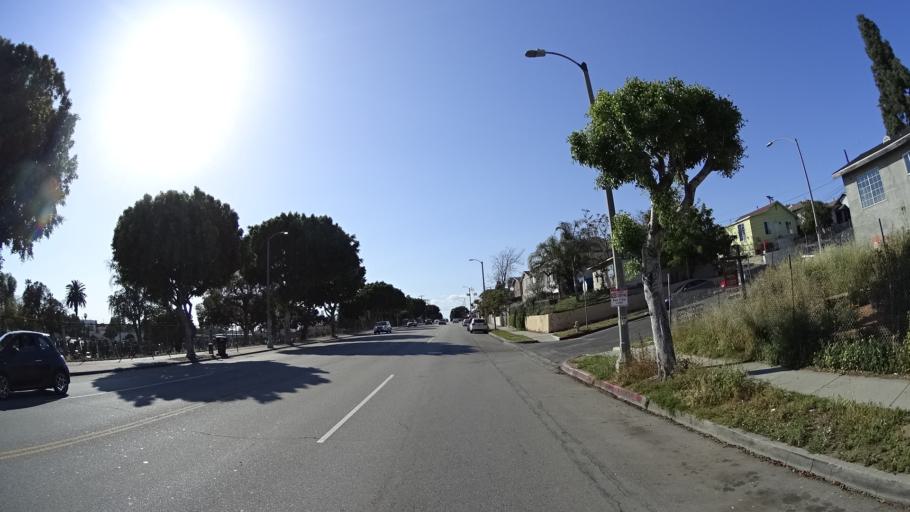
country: US
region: California
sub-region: Los Angeles County
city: Boyle Heights
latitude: 34.0427
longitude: -118.1984
